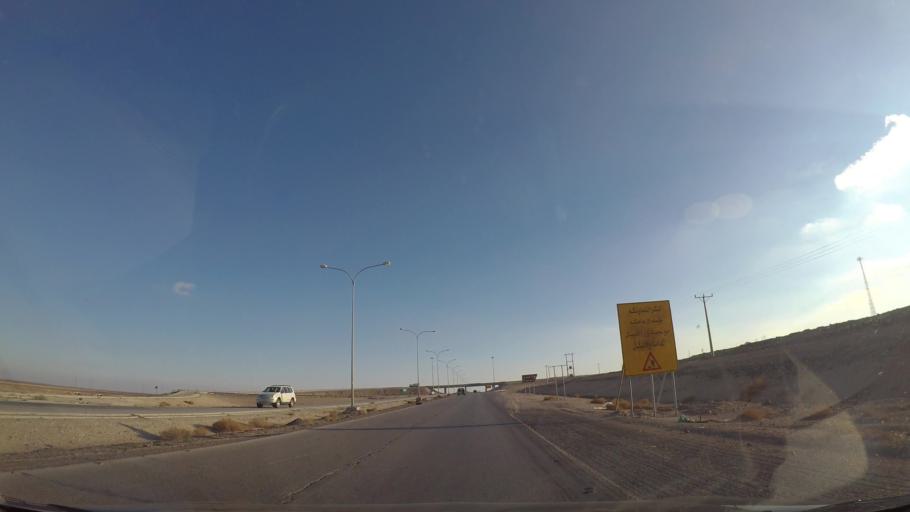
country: JO
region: Tafielah
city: Busayra
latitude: 30.5018
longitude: 35.7996
